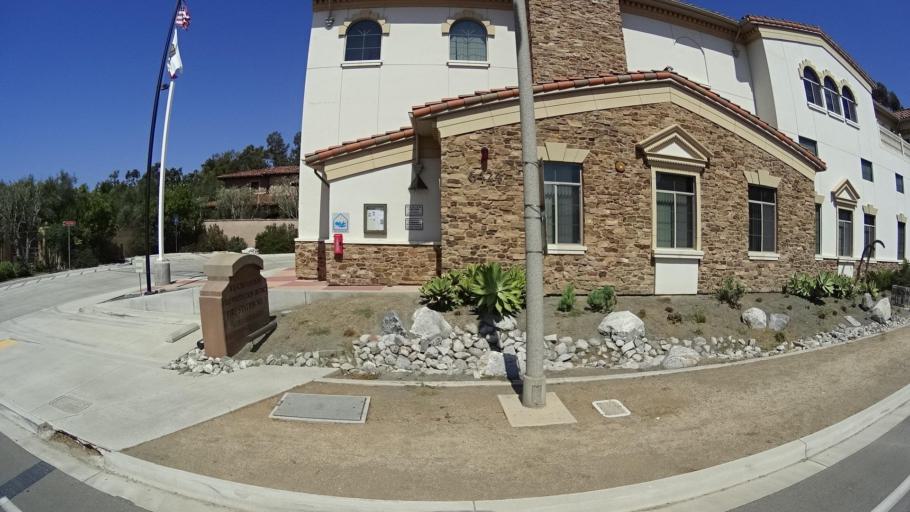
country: US
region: California
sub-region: San Diego County
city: Fairbanks Ranch
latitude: 32.9977
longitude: -117.1946
